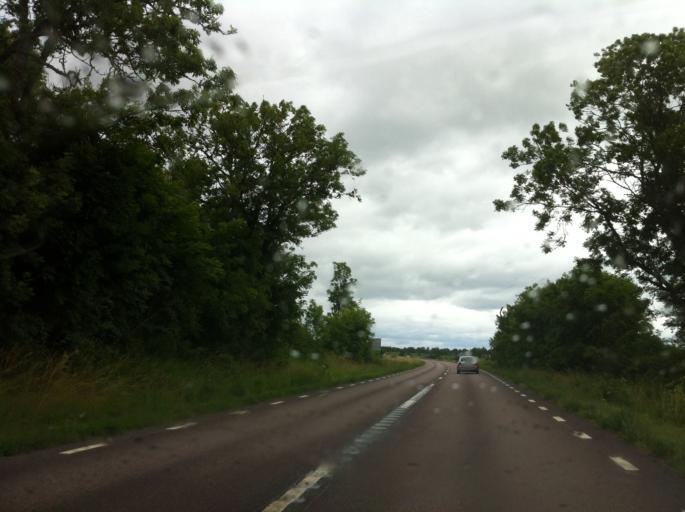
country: SE
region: Kalmar
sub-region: Borgholms Kommun
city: Borgholm
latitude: 57.1215
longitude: 16.9649
